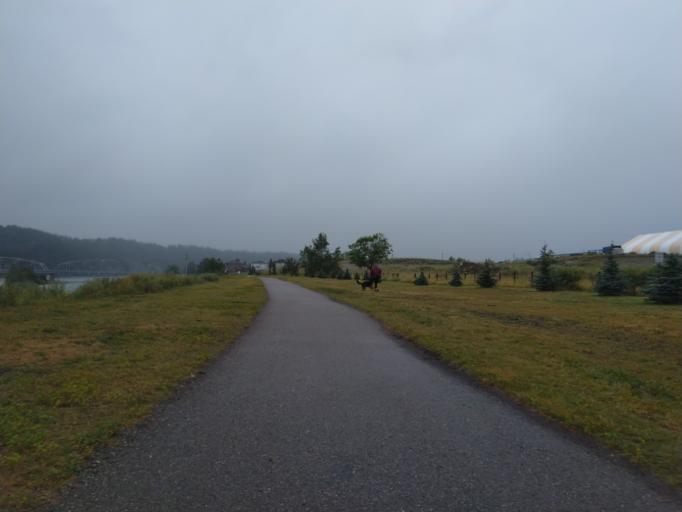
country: CA
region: Alberta
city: Cochrane
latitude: 51.1742
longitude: -114.4616
